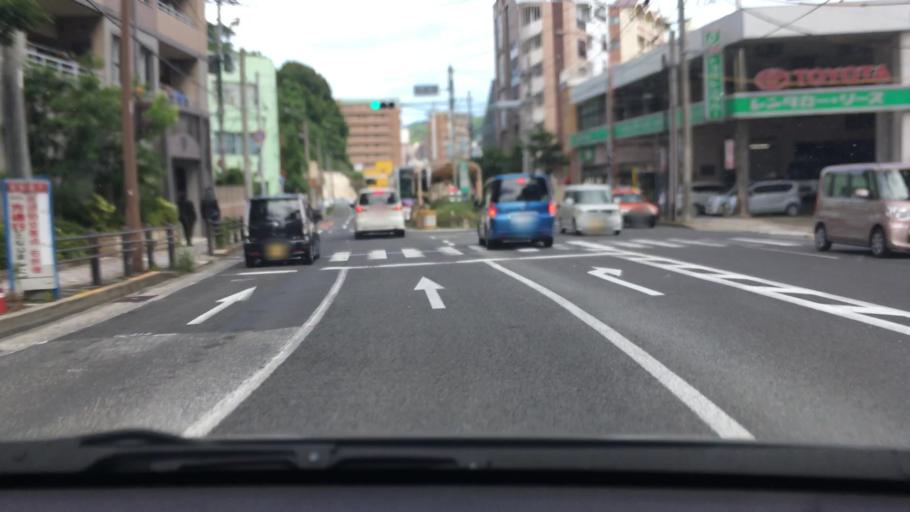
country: JP
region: Nagasaki
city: Obita
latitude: 32.7943
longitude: 129.8568
